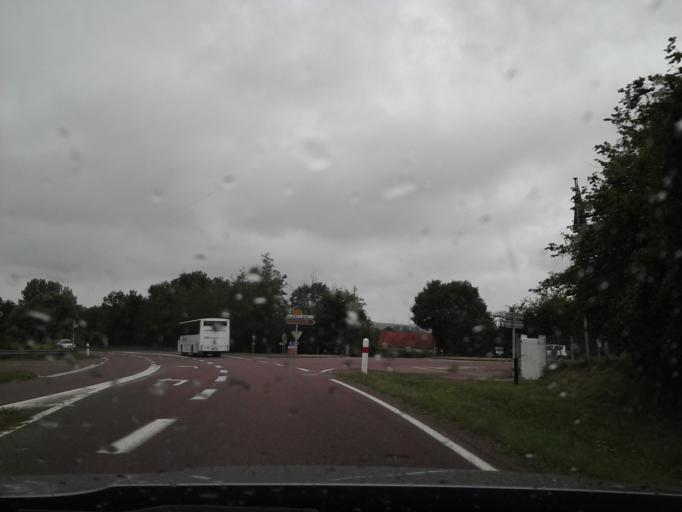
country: FR
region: Lower Normandy
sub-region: Departement de la Manche
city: Carentan
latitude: 49.3287
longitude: -1.2682
